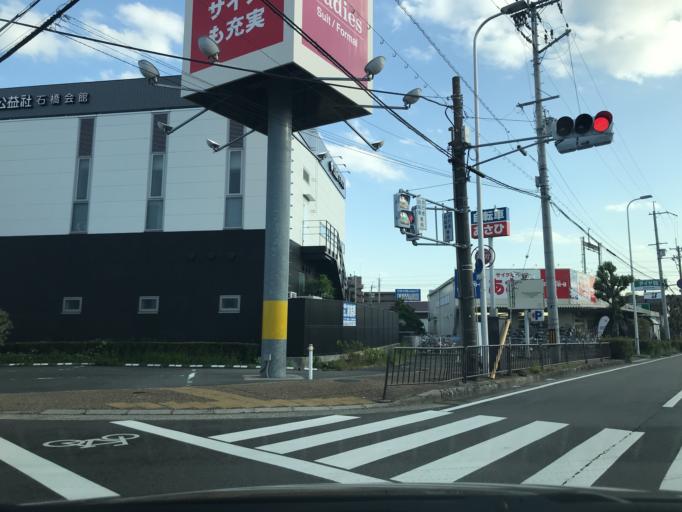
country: JP
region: Osaka
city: Ikeda
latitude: 34.8128
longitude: 135.4412
